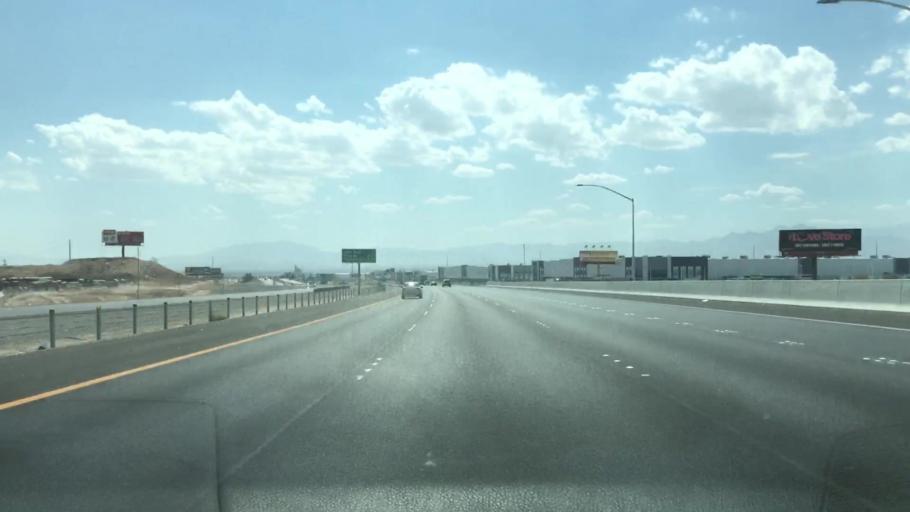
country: US
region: Nevada
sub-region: Clark County
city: Nellis Air Force Base
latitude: 36.2675
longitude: -115.0672
